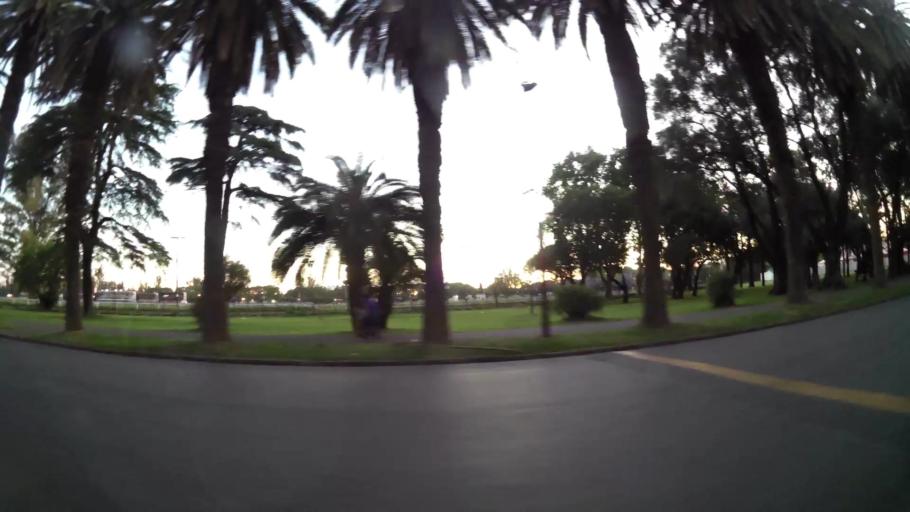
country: AR
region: Santa Fe
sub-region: Departamento de Rosario
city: Rosario
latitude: -32.9567
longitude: -60.6623
